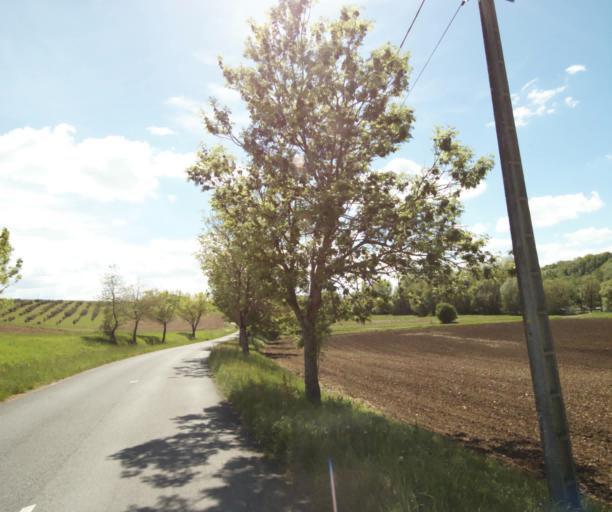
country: FR
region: Poitou-Charentes
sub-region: Departement de la Charente-Maritime
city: Chaniers
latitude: 45.7329
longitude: -0.5076
